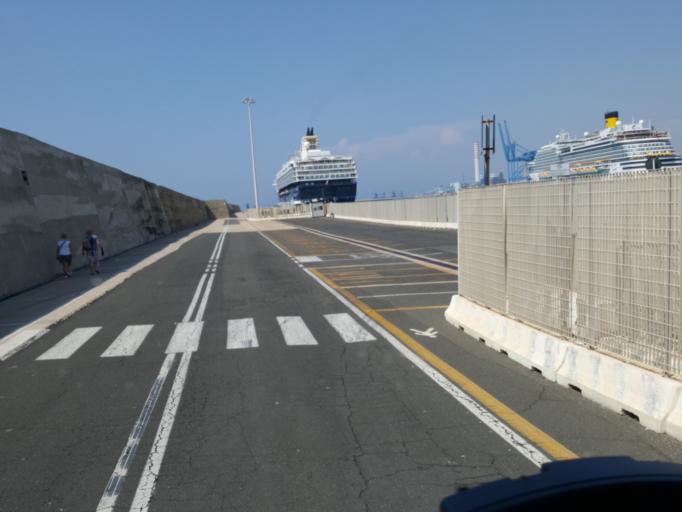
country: IT
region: Latium
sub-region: Citta metropolitana di Roma Capitale
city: Civitavecchia
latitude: 42.0971
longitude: 11.7760
